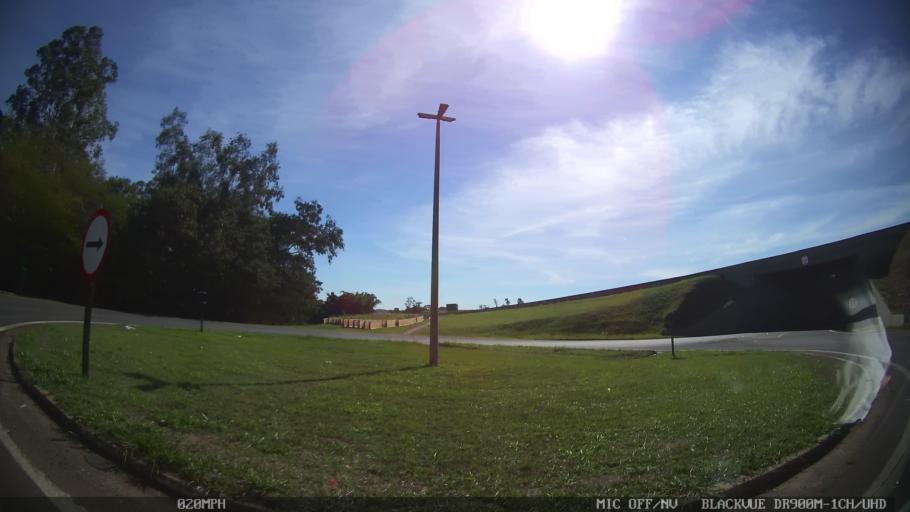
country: BR
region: Sao Paulo
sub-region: Pirassununga
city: Pirassununga
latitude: -22.0741
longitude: -47.4238
